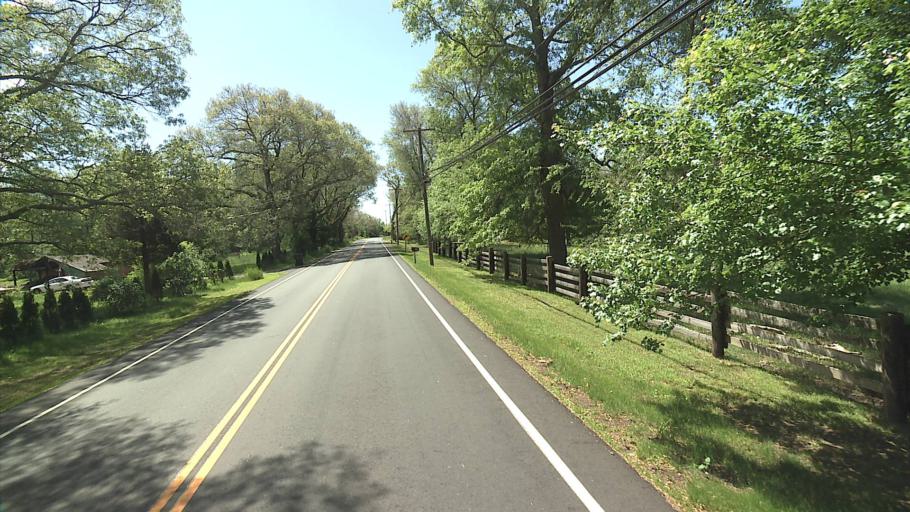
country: US
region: Connecticut
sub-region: Windham County
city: Moosup
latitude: 41.6861
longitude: -71.8494
